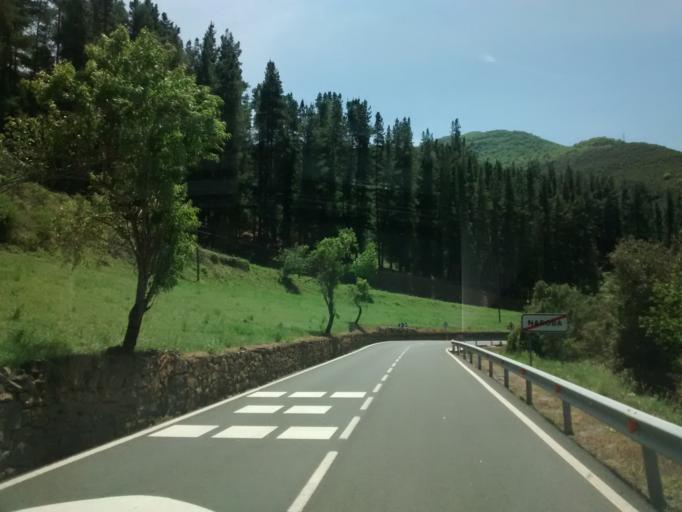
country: ES
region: Cantabria
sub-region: Provincia de Cantabria
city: Potes
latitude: 43.1204
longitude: -4.6287
